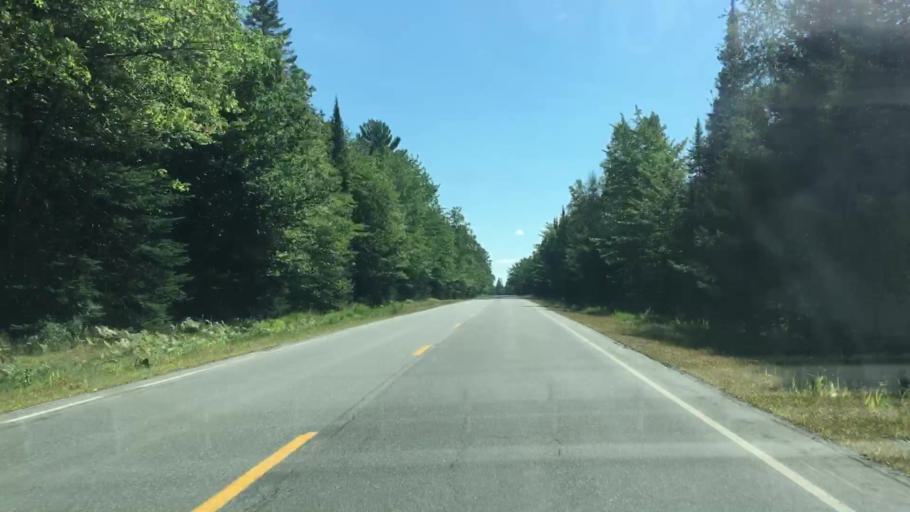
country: US
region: Maine
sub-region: Piscataquis County
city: Milo
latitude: 45.2067
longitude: -68.9089
